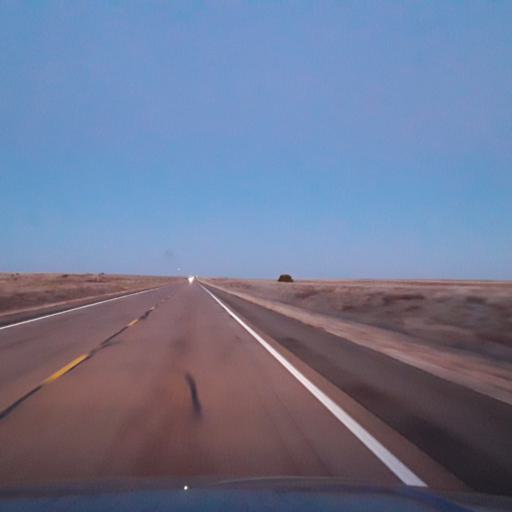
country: US
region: New Mexico
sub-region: Guadalupe County
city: Santa Rosa
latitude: 34.7601
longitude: -104.9900
